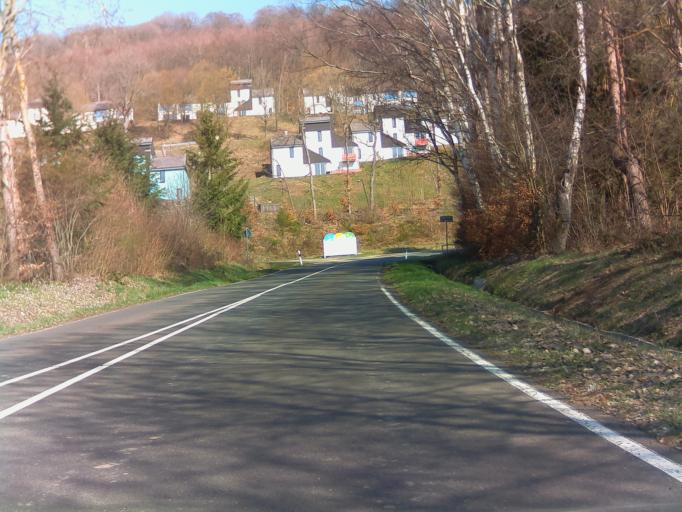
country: DE
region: Rheinland-Pfalz
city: Hattgenstein
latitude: 49.6873
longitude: 7.1477
